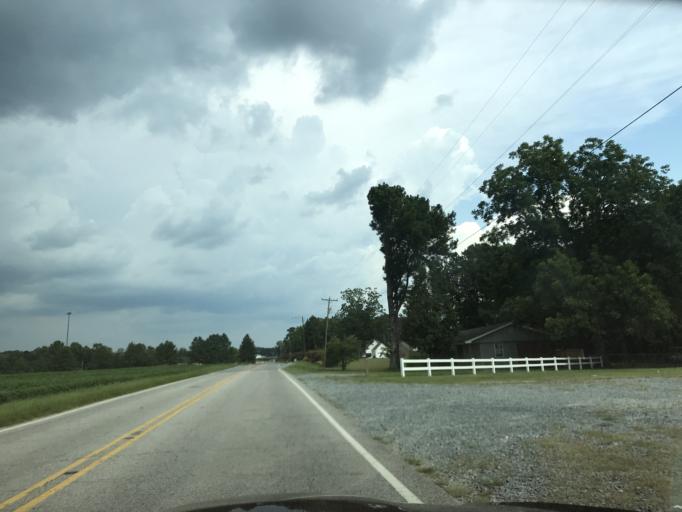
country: US
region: North Carolina
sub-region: Johnston County
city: Four Oaks
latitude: 35.5111
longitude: -78.5268
